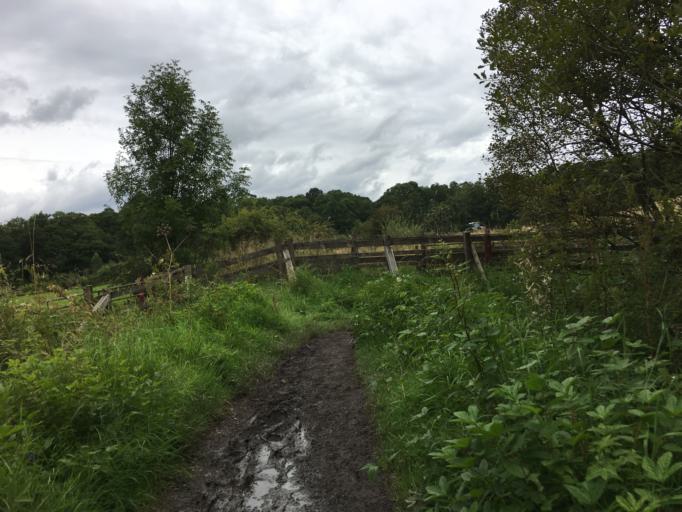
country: GB
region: Scotland
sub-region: Stirling
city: Killearn
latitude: 56.0353
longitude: -4.3920
